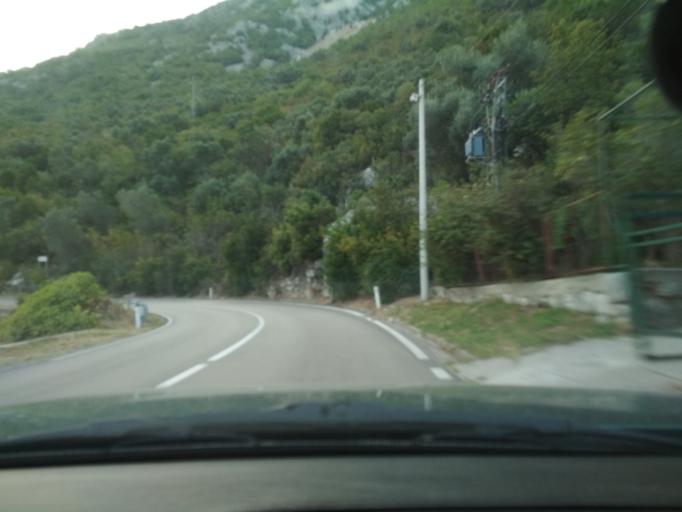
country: ME
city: Lipci
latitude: 42.5047
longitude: 18.6686
